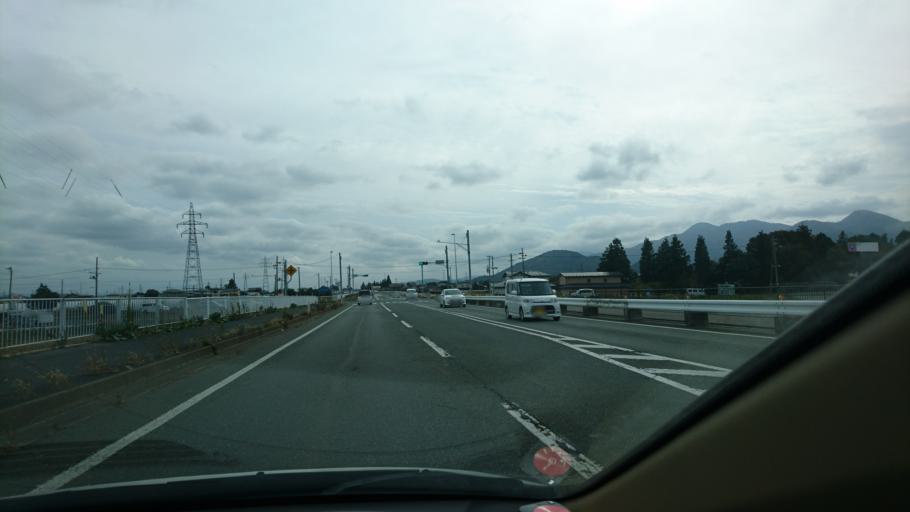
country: JP
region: Iwate
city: Morioka-shi
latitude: 39.7013
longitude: 141.1031
